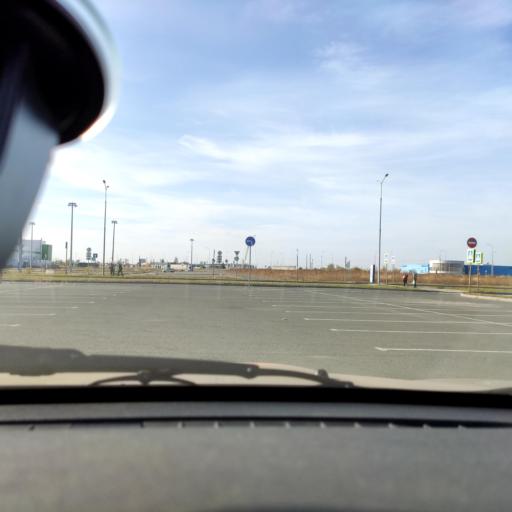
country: RU
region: Samara
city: Tol'yatti
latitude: 53.5515
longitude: 49.3435
